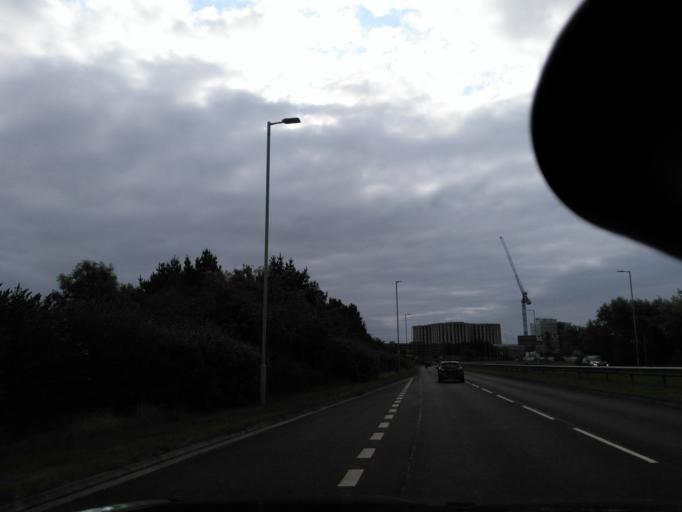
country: GB
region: England
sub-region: Poole
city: Poole
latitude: 50.7229
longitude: -1.9892
